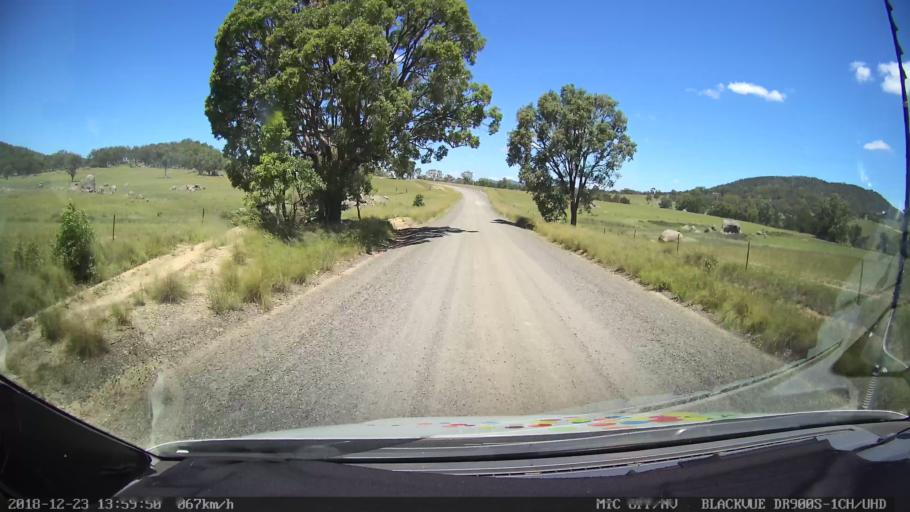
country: AU
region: New South Wales
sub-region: Tamworth Municipality
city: Manilla
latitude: -30.6113
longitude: 151.0988
